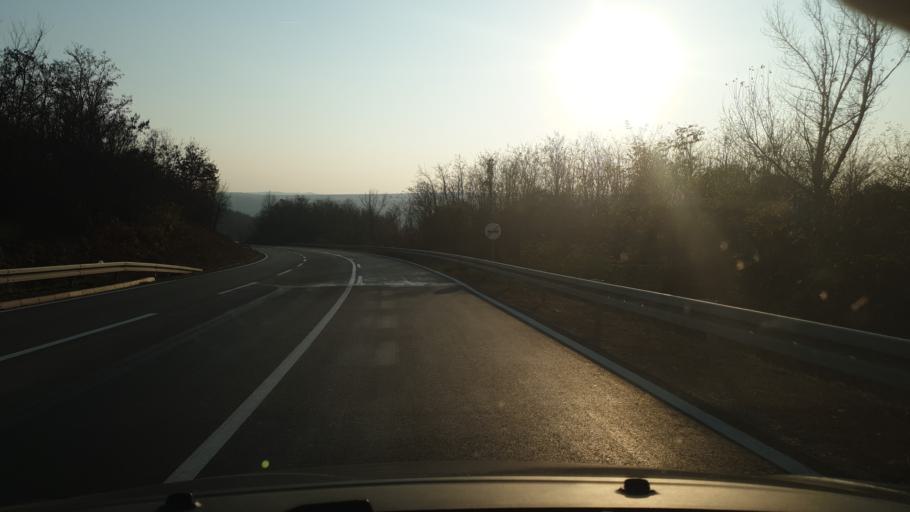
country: RS
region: Central Serbia
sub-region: Zajecarski Okrug
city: Zajecar
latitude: 43.9911
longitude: 22.2997
